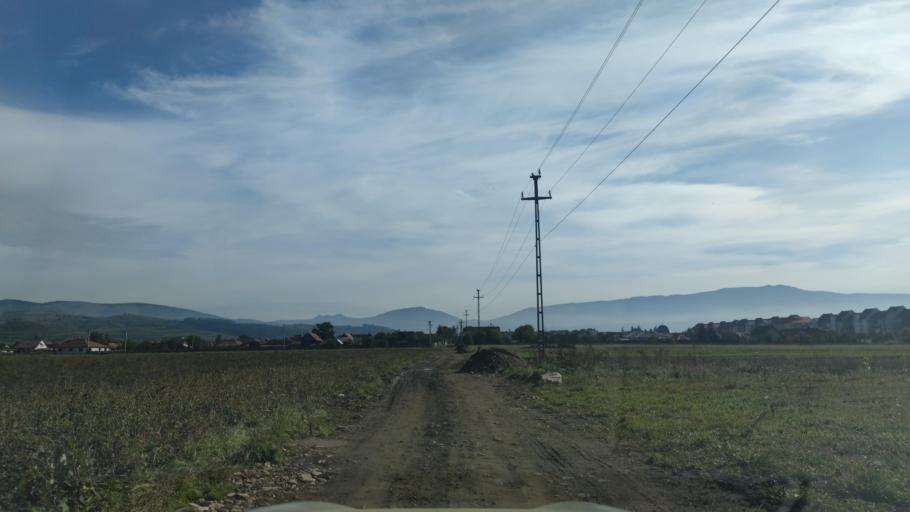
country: RO
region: Harghita
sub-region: Municipiul Gheorgheni
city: Gheorgheni
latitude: 46.7234
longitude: 25.5799
